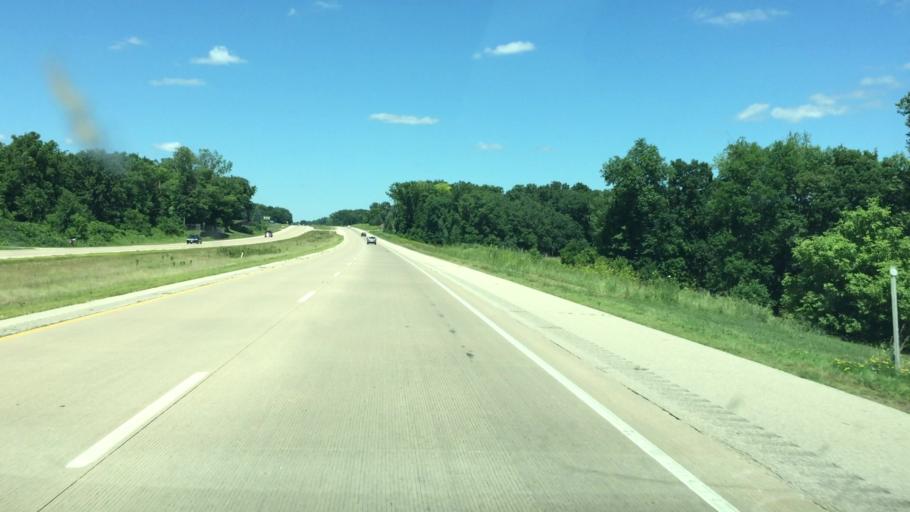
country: US
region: Wisconsin
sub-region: Grant County
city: Dickeyville
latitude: 42.6799
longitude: -90.5400
